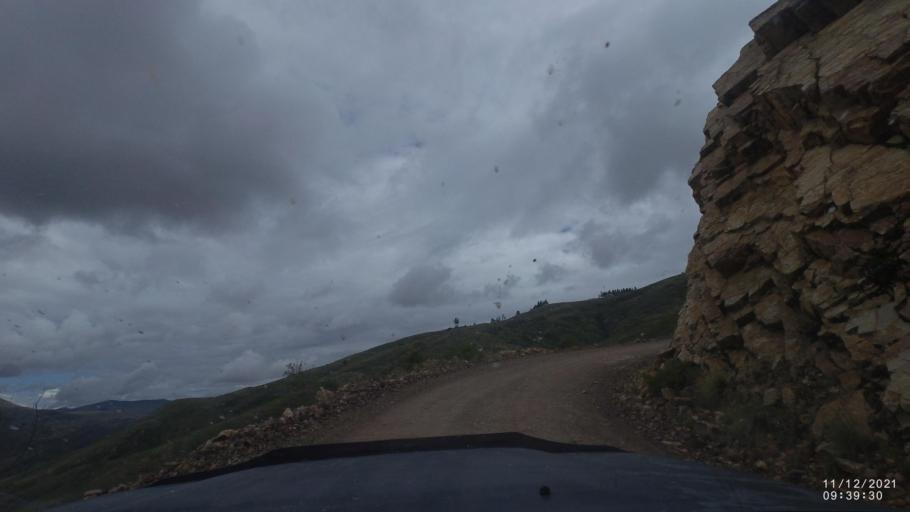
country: BO
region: Cochabamba
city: Tarata
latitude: -17.8155
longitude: -65.9847
